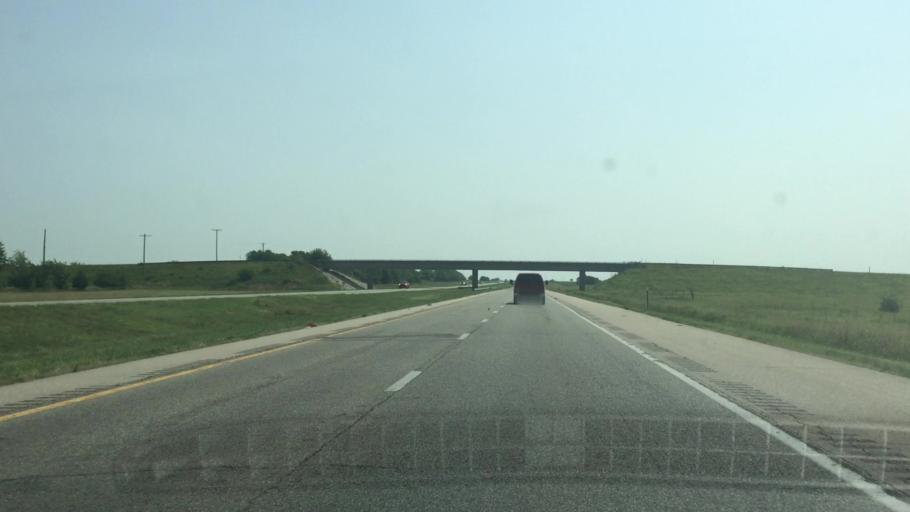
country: US
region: Kansas
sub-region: Osage County
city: Osage City
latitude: 38.4257
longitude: -95.8218
